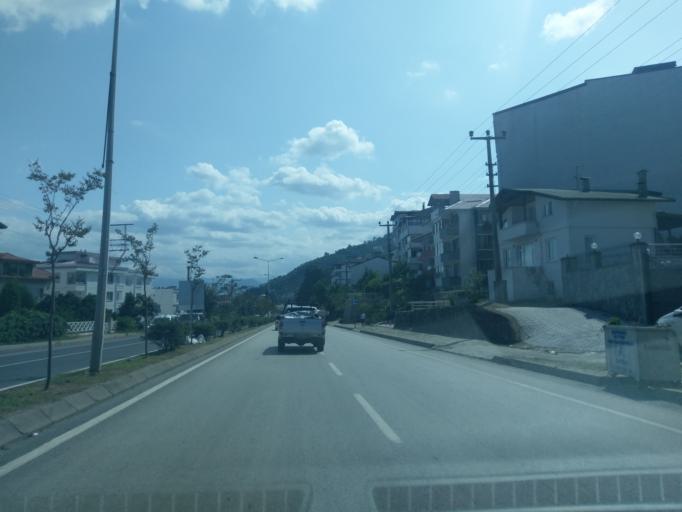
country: TR
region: Ordu
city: Ordu
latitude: 41.0084
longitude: 37.8688
